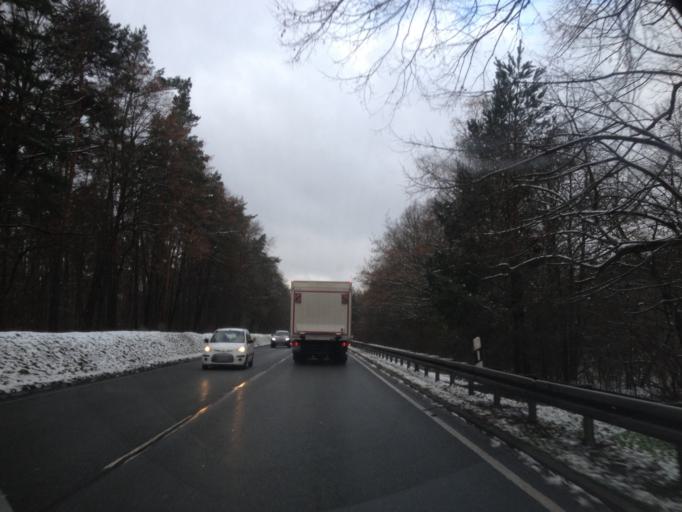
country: DE
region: Bavaria
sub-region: Regierungsbezirk Mittelfranken
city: Schwaig
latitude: 49.4747
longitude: 11.1588
